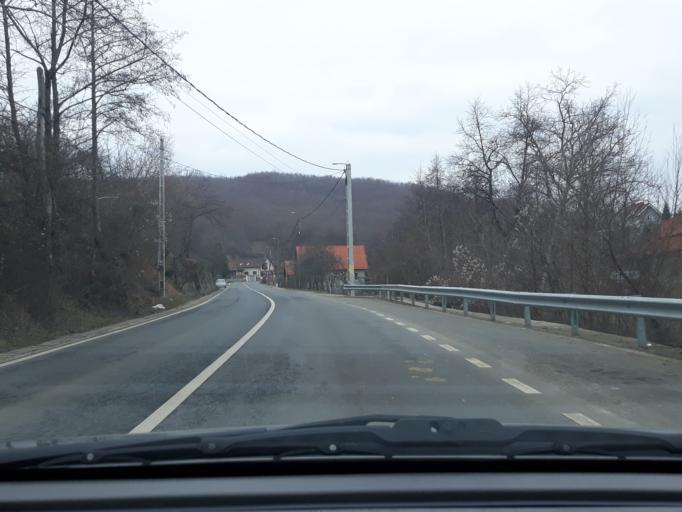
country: RO
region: Bihor
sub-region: Oras Alesd
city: Pestis
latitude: 47.0784
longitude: 22.4110
